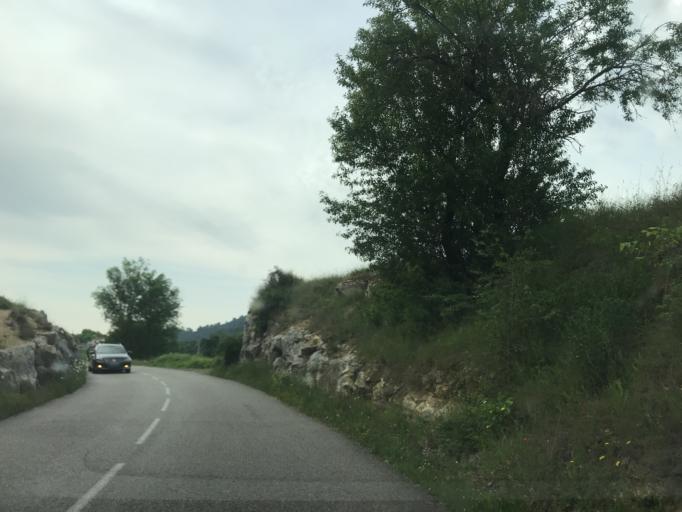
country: FR
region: Provence-Alpes-Cote d'Azur
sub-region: Departement du Vaucluse
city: Beaumont-de-Pertuis
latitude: 43.6851
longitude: 5.7111
